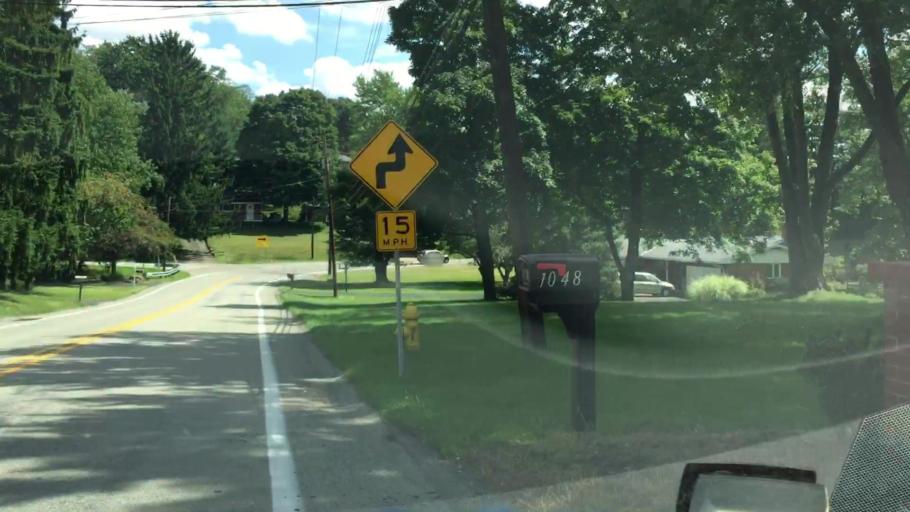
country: US
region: Pennsylvania
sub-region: Allegheny County
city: Bethel Park
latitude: 40.3164
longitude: -80.0420
